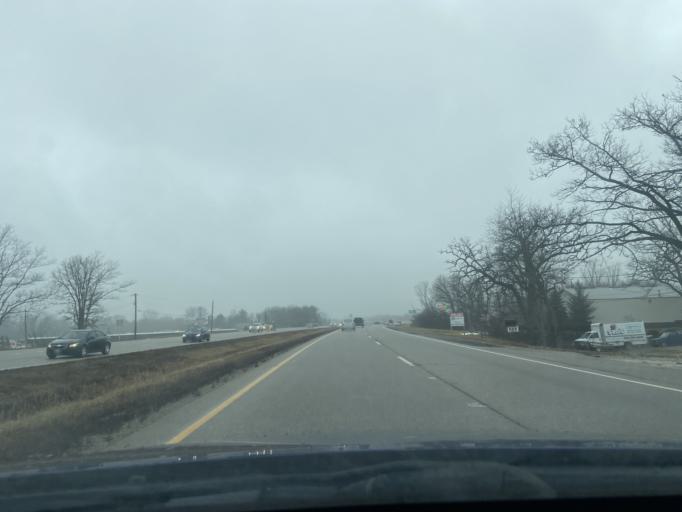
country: US
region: Illinois
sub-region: Lake County
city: Wauconda
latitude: 42.2531
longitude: -88.1488
